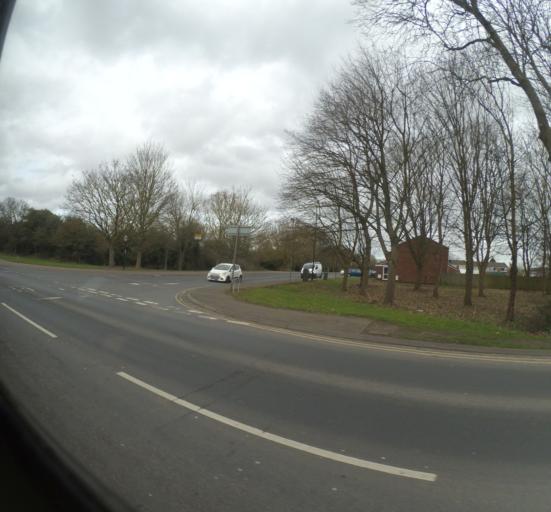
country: GB
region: England
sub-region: Warwickshire
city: Ryton on Dunsmore
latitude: 52.4185
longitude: -1.4463
